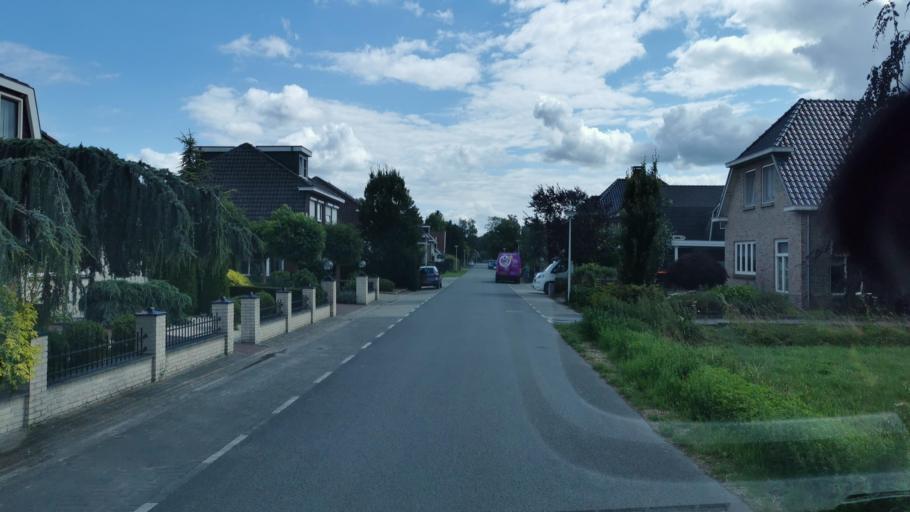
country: NL
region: Overijssel
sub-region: Gemeente Losser
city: Losser
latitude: 52.2259
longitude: 6.9729
